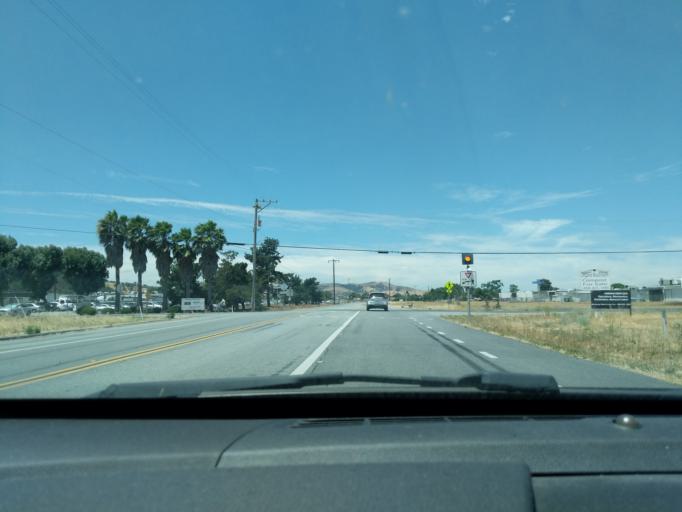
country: US
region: California
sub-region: Santa Clara County
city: Morgan Hill
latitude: 37.1640
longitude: -121.7031
